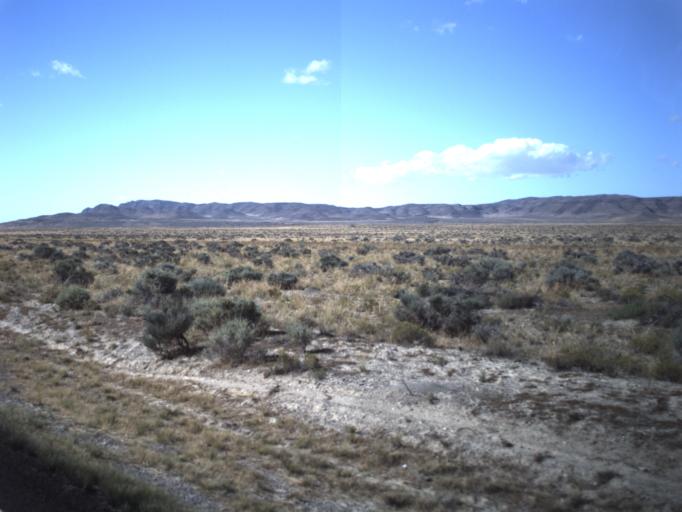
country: US
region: Utah
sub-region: Millard County
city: Delta
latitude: 38.9257
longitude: -112.8109
